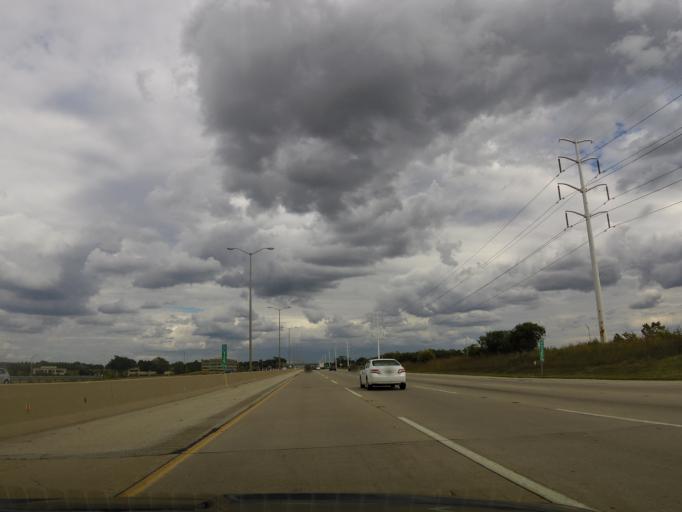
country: US
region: Illinois
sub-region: DuPage County
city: Warrenville
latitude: 41.8064
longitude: -88.1670
